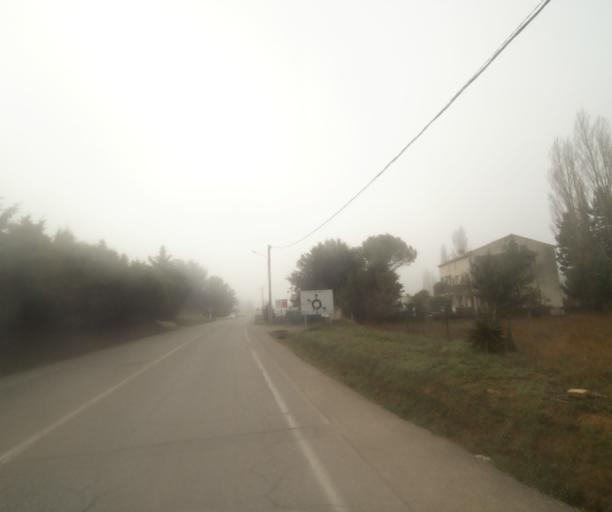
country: FR
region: Provence-Alpes-Cote d'Azur
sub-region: Departement des Bouches-du-Rhone
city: Eguilles
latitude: 43.5445
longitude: 5.3681
